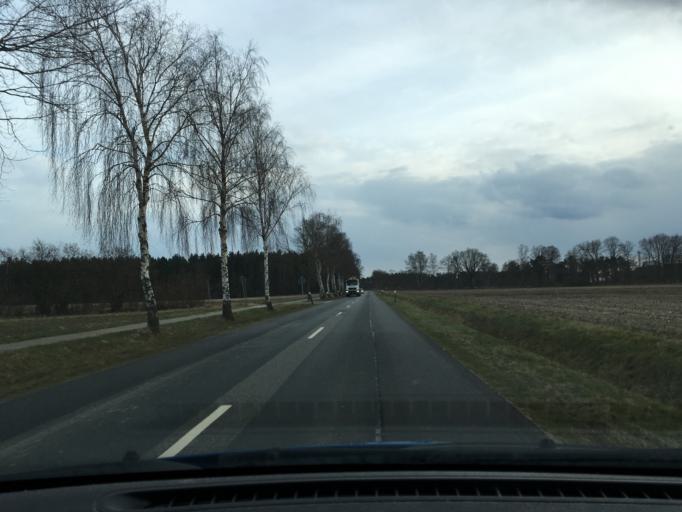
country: DE
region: Lower Saxony
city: Vogelsen
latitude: 53.2695
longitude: 10.3434
